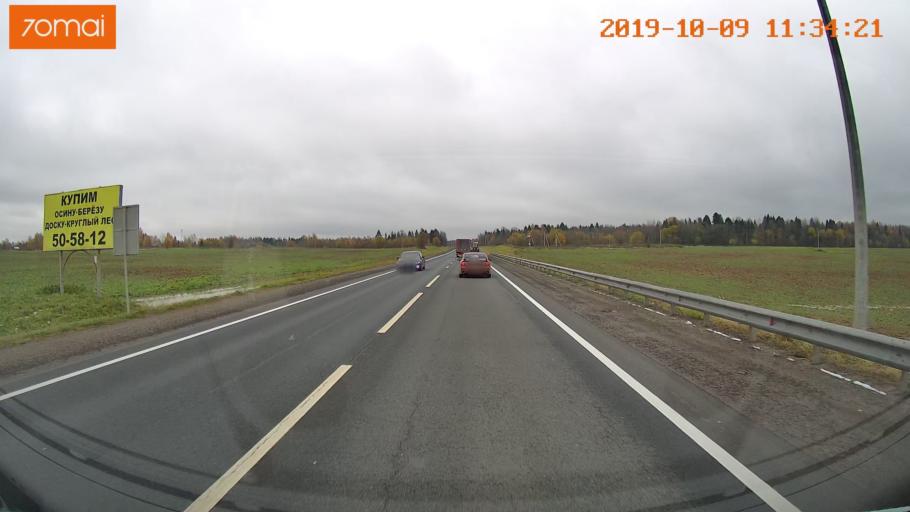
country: RU
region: Vologda
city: Gryazovets
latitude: 59.0174
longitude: 40.1178
